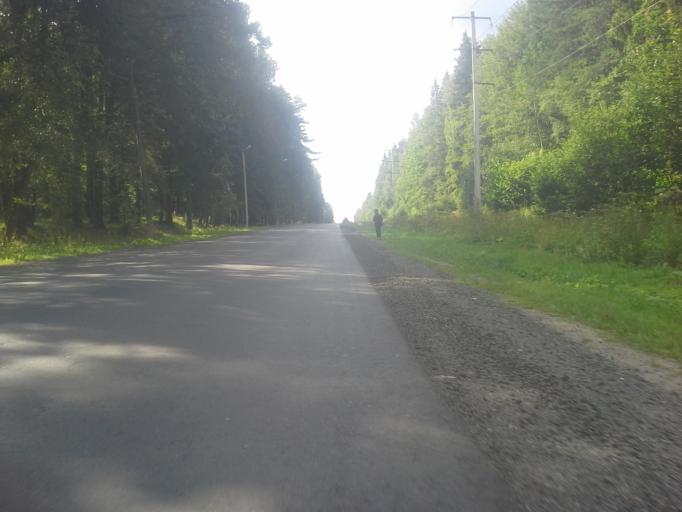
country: RU
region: Moskovskaya
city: Troitsk
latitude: 55.3228
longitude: 37.1375
